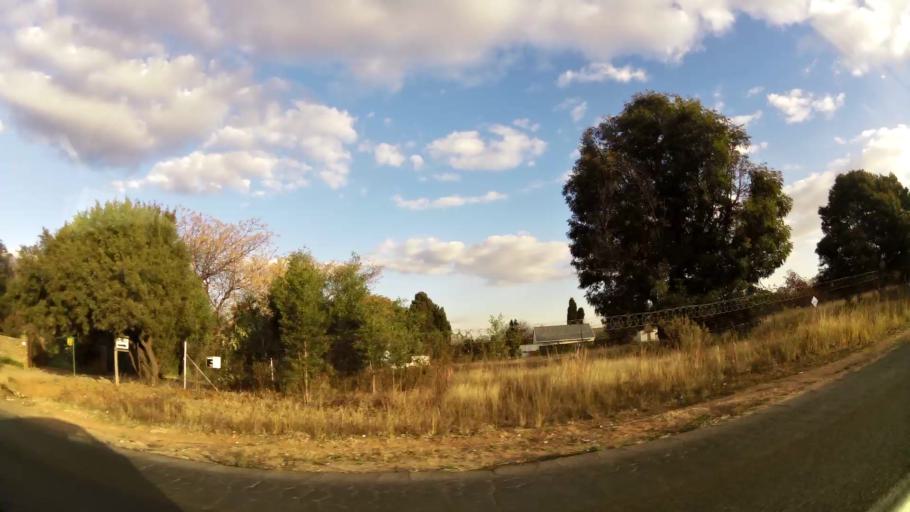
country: ZA
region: Gauteng
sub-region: City of Johannesburg Metropolitan Municipality
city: Midrand
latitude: -25.9578
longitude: 28.1617
